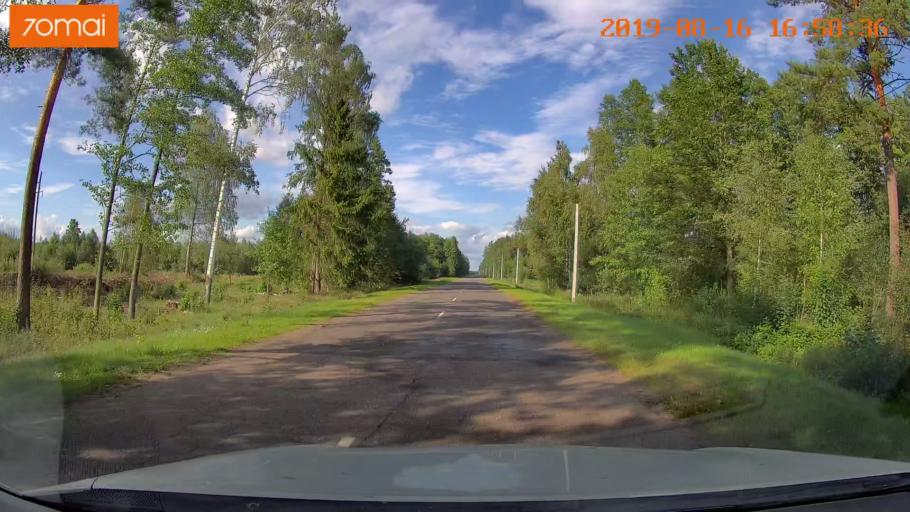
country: BY
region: Mogilev
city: Hlusha
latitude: 53.2716
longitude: 28.8348
